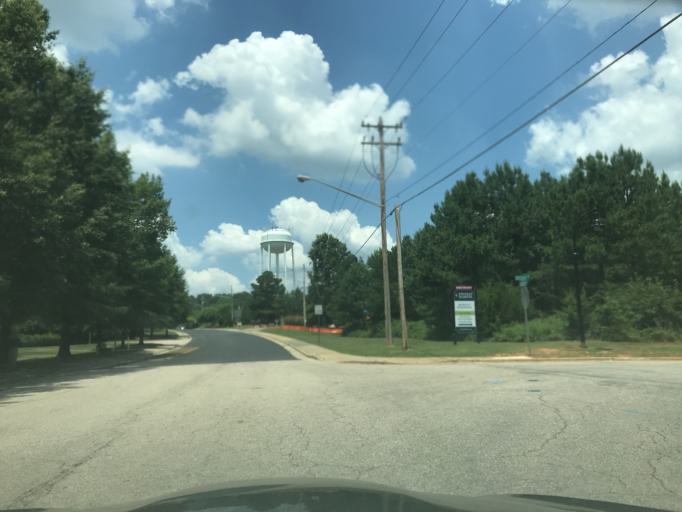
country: US
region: North Carolina
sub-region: Wake County
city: Wake Forest
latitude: 35.9704
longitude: -78.5104
